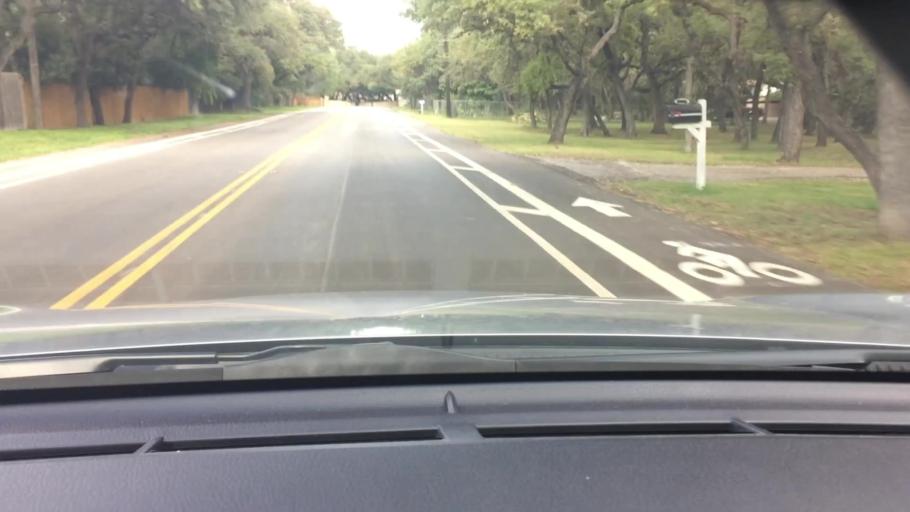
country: US
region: Texas
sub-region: Bexar County
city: Shavano Park
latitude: 29.5597
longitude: -98.5450
